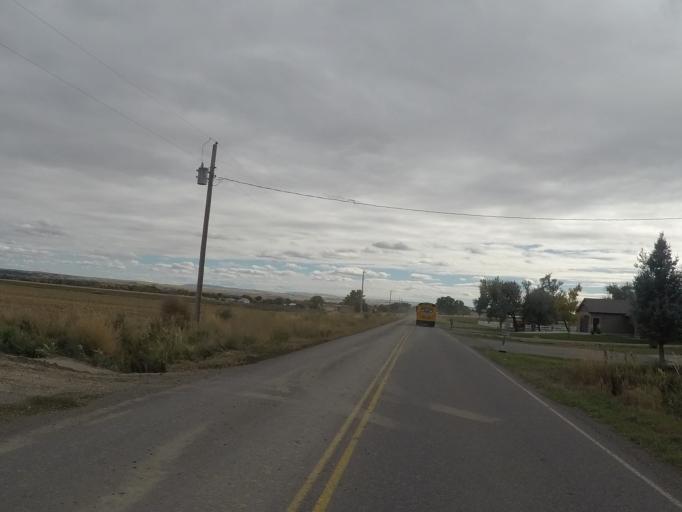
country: US
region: Montana
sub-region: Yellowstone County
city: Laurel
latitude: 45.7481
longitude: -108.6589
